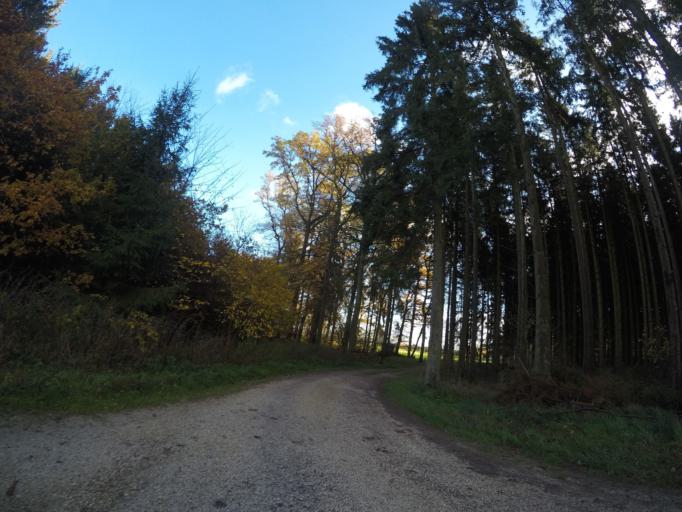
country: DE
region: Baden-Wuerttemberg
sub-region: Tuebingen Region
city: Bernstadt
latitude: 48.4560
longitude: 10.0202
